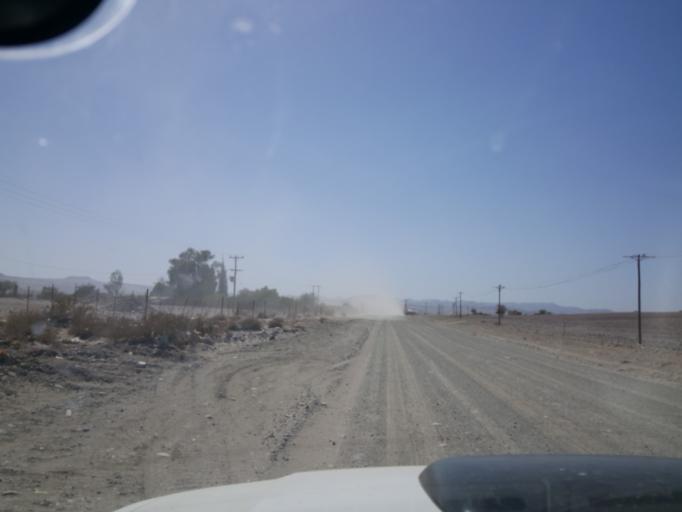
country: ZA
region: Northern Cape
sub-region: Namakwa District Municipality
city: Port Nolloth
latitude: -28.6983
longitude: 17.5891
